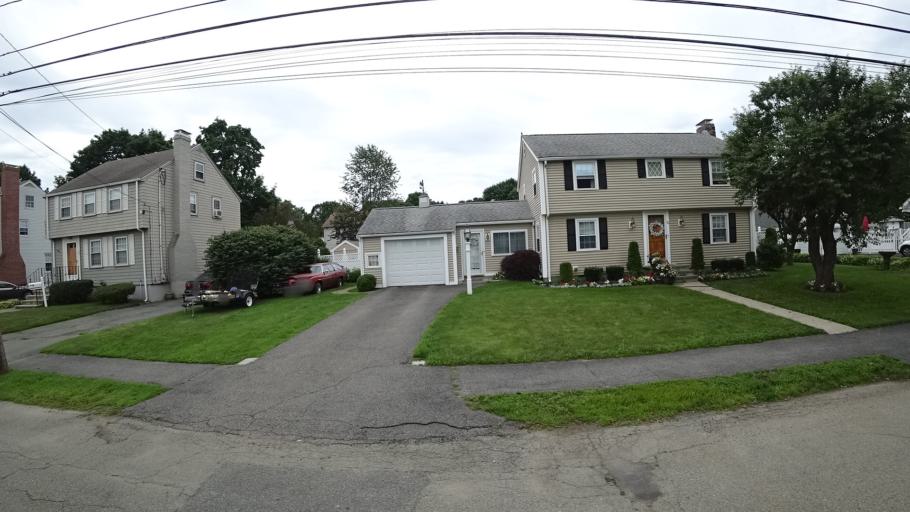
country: US
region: Massachusetts
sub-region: Norfolk County
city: Dedham
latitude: 42.2329
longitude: -71.1547
